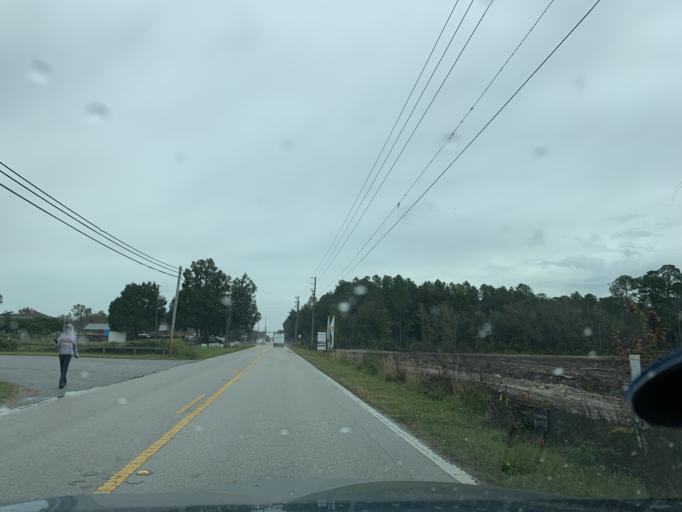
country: US
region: Florida
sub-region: Pasco County
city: Wesley Chapel
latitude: 28.2537
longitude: -82.3201
